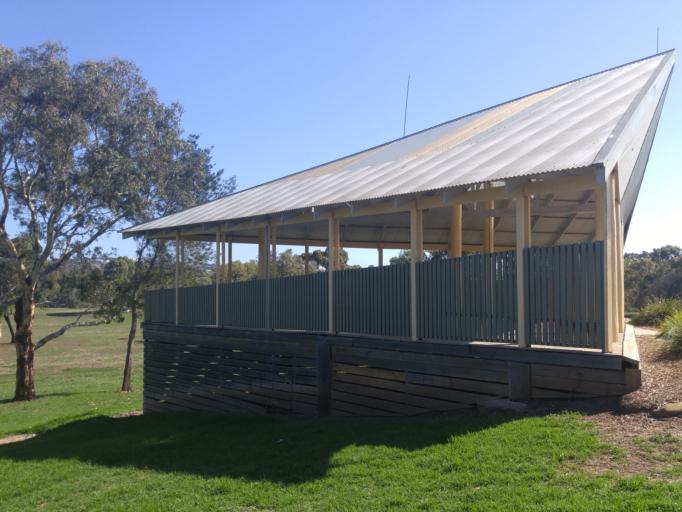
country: AU
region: Victoria
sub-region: Greater Geelong
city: Hamlyn Heights
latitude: -38.1424
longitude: 144.3110
